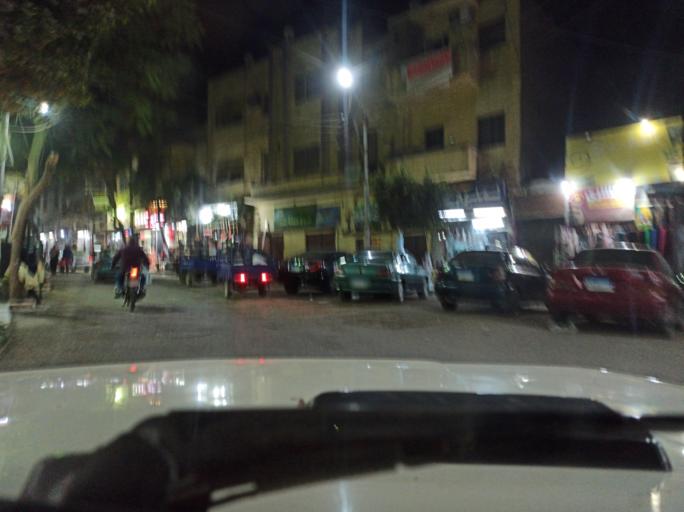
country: EG
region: Muhafazat Bani Suwayf
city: Bani Suwayf
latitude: 29.0744
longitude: 31.0937
